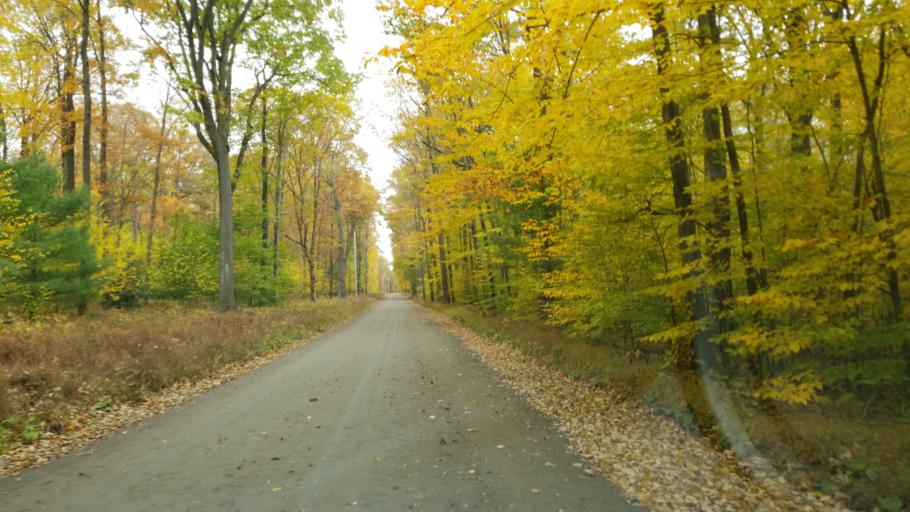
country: US
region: Pennsylvania
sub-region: Clearfield County
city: Shiloh
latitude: 41.1893
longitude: -78.3713
